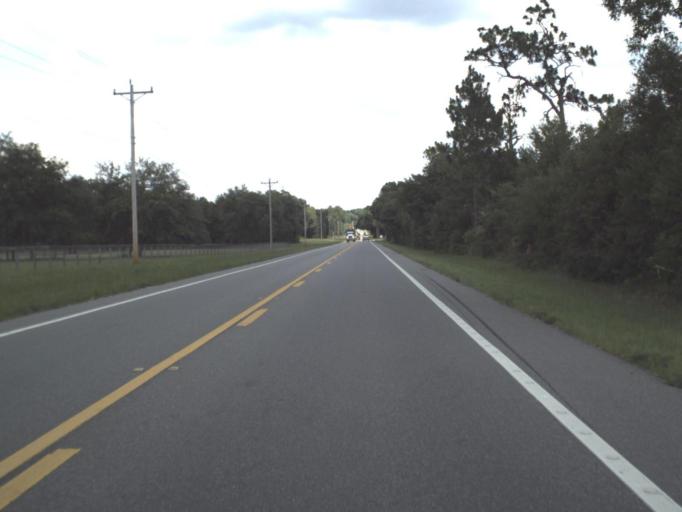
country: US
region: Florida
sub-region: Clay County
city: Keystone Heights
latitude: 29.7430
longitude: -81.9752
